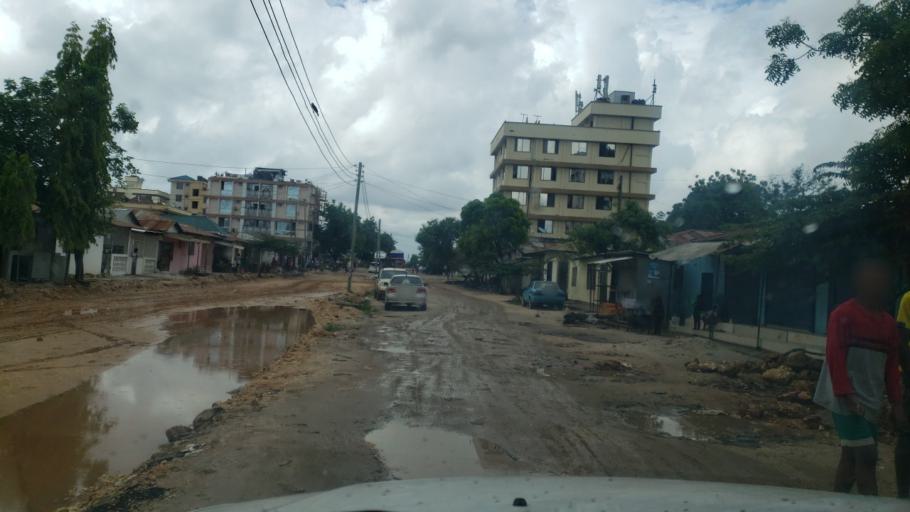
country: TZ
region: Dar es Salaam
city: Magomeni
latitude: -6.8108
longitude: 39.2594
